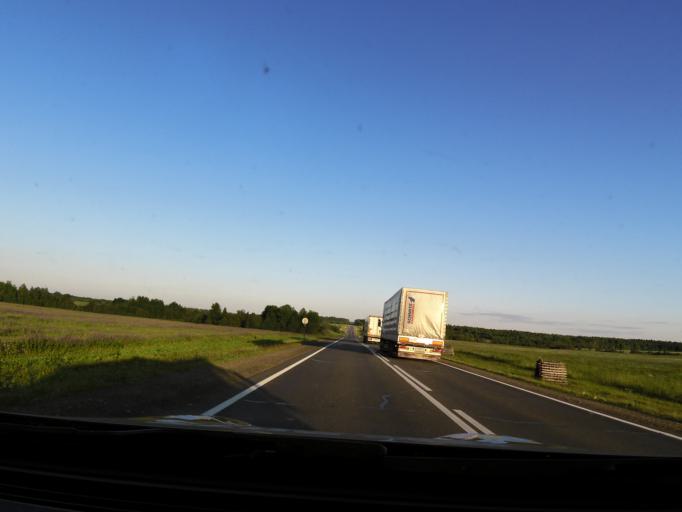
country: RU
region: Vologda
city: Gryazovets
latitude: 58.8270
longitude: 40.2191
